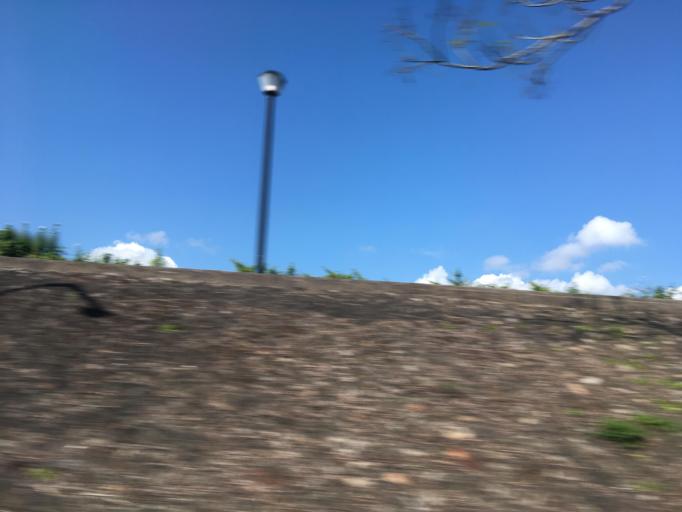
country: TW
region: Taiwan
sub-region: Yilan
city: Yilan
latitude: 24.7577
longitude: 121.7328
